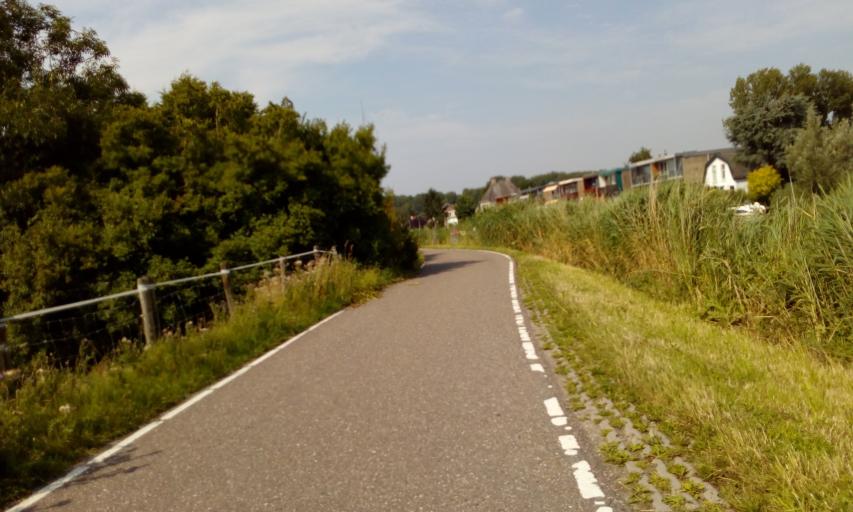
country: NL
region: South Holland
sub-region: Gemeente Lansingerland
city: Bergschenhoek
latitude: 51.9652
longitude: 4.5273
